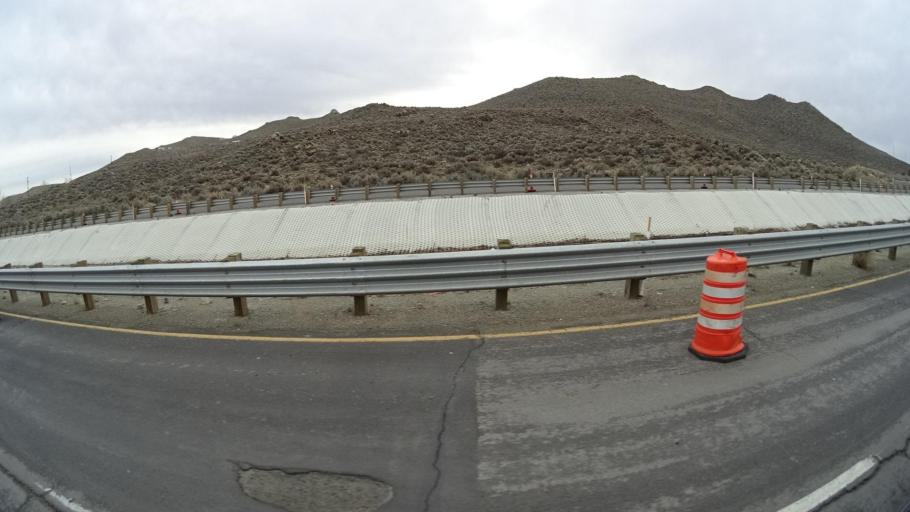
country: US
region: Nevada
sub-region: Washoe County
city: Lemmon Valley
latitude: 39.6269
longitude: -119.8473
